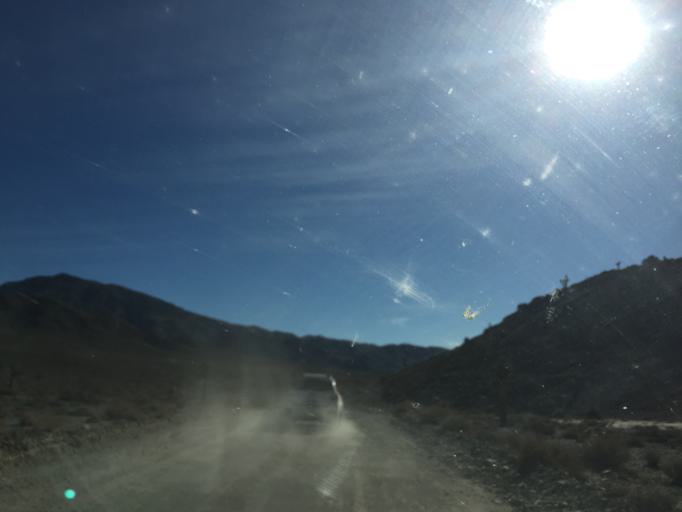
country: US
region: California
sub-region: Inyo County
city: Lone Pine
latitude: 36.8154
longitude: -117.5103
